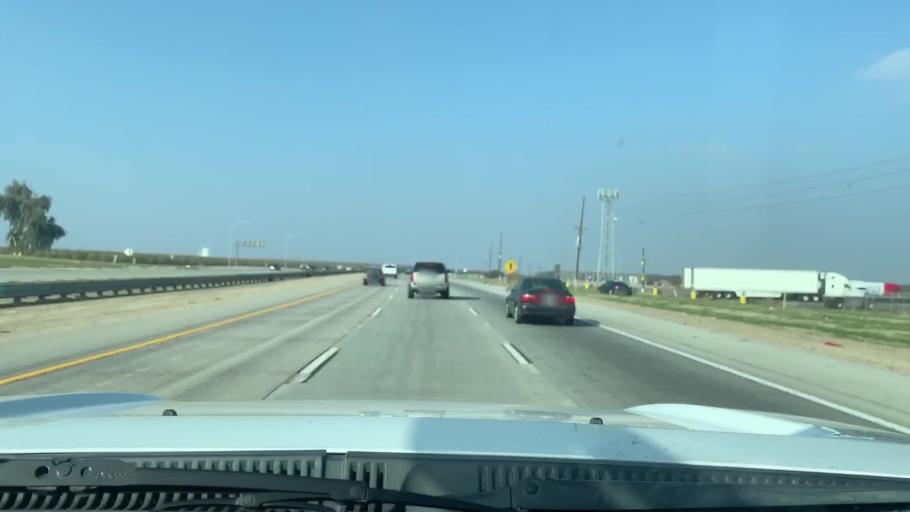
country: US
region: California
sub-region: Kern County
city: Shafter
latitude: 35.5311
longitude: -119.1901
